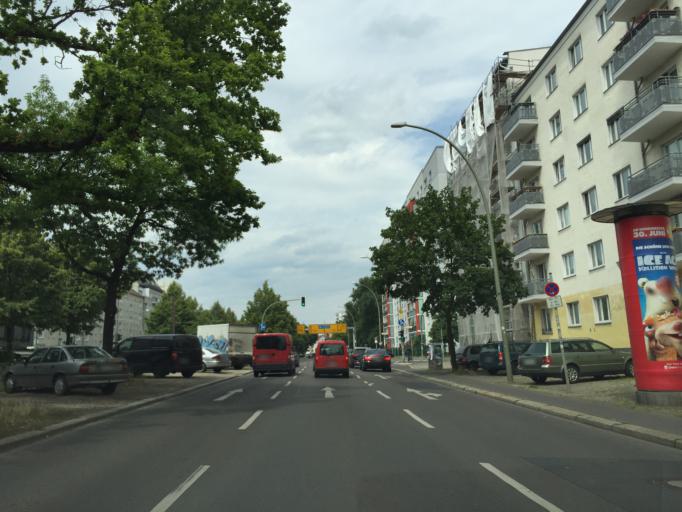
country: DE
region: Berlin
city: Friedrichshain Bezirk
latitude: 52.5238
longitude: 13.4496
